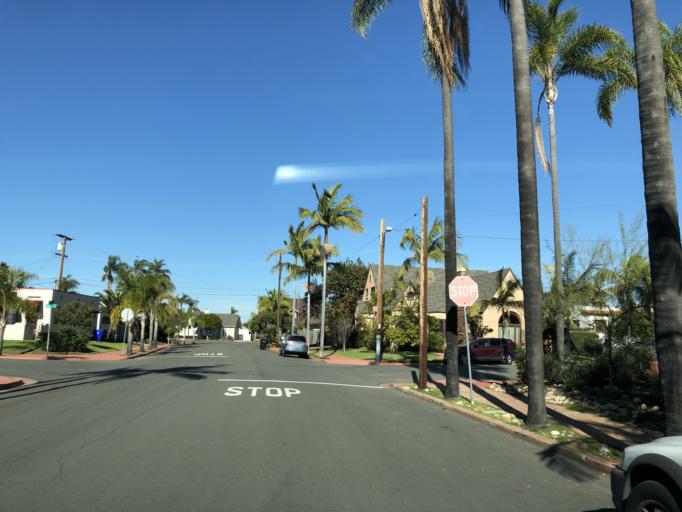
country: US
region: California
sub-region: San Diego County
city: San Diego
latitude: 32.7315
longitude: -117.1261
